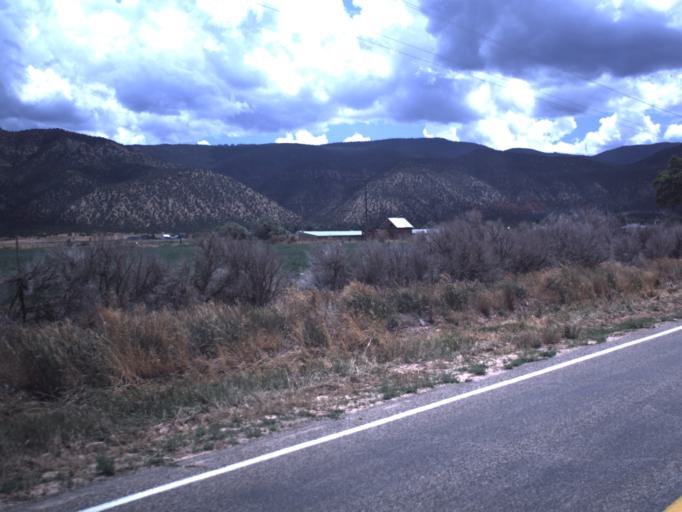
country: US
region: Utah
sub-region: Iron County
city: Parowan
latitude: 37.8979
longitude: -112.7749
